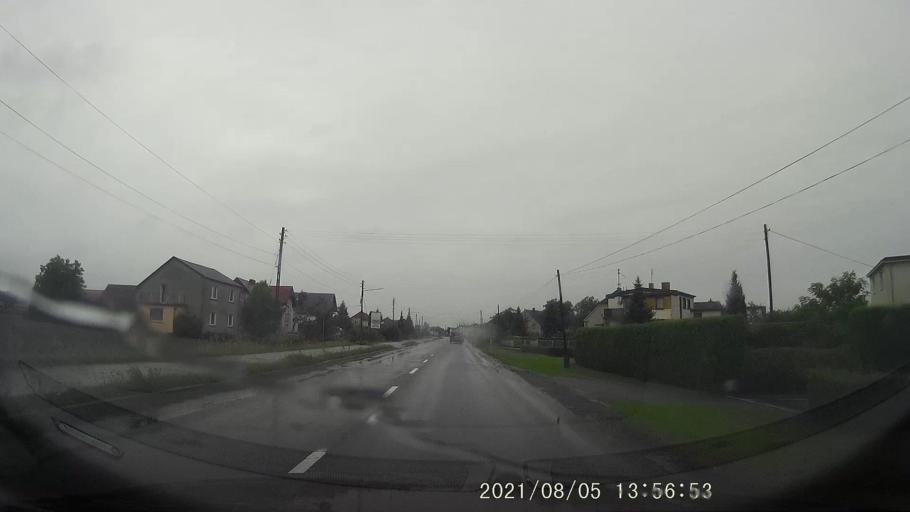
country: PL
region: Opole Voivodeship
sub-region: Powiat krapkowicki
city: Krapkowice
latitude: 50.4614
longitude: 17.9402
